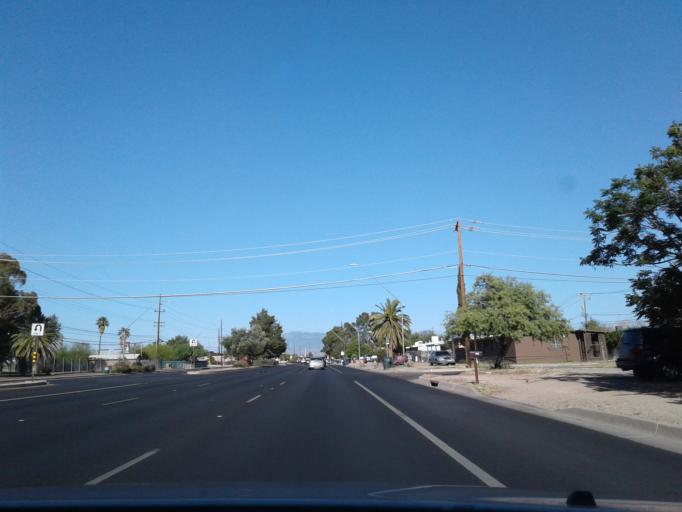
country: US
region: Arizona
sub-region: Pima County
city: Tucson
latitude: 32.2069
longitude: -110.9142
